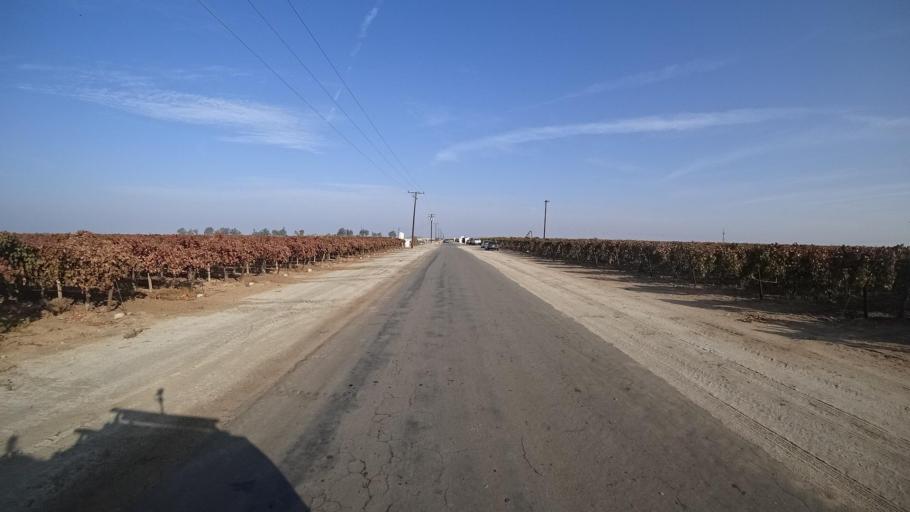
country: US
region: California
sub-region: Kern County
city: McFarland
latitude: 35.6812
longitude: -119.1871
